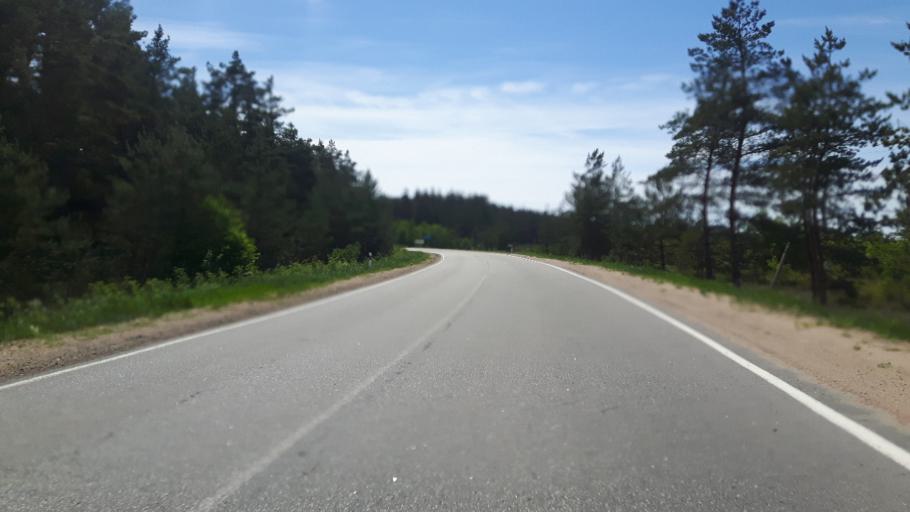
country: EE
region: Ida-Virumaa
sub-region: Narva-Joesuu linn
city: Narva-Joesuu
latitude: 59.5698
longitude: 28.1540
